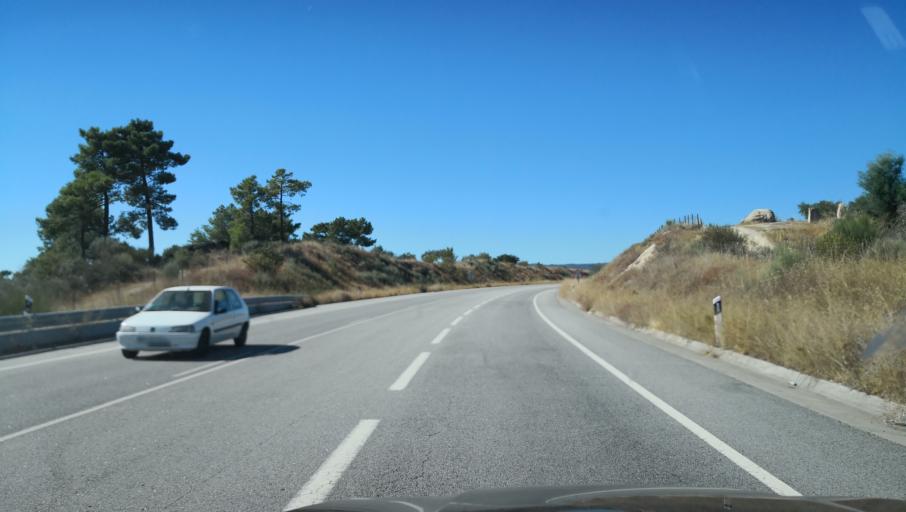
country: PT
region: Vila Real
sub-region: Valpacos
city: Valpacos
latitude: 41.5713
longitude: -7.2963
